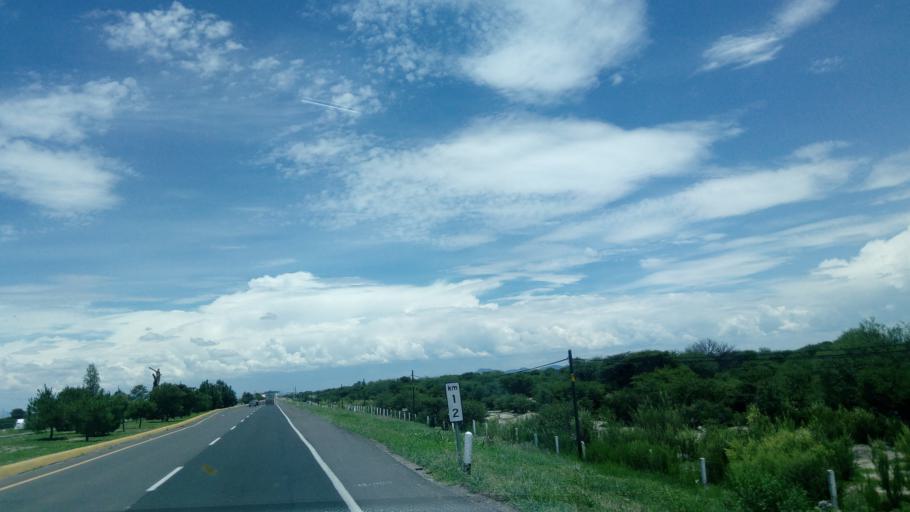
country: MX
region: Durango
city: Victoria de Durango
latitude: 24.1054
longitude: -104.5602
